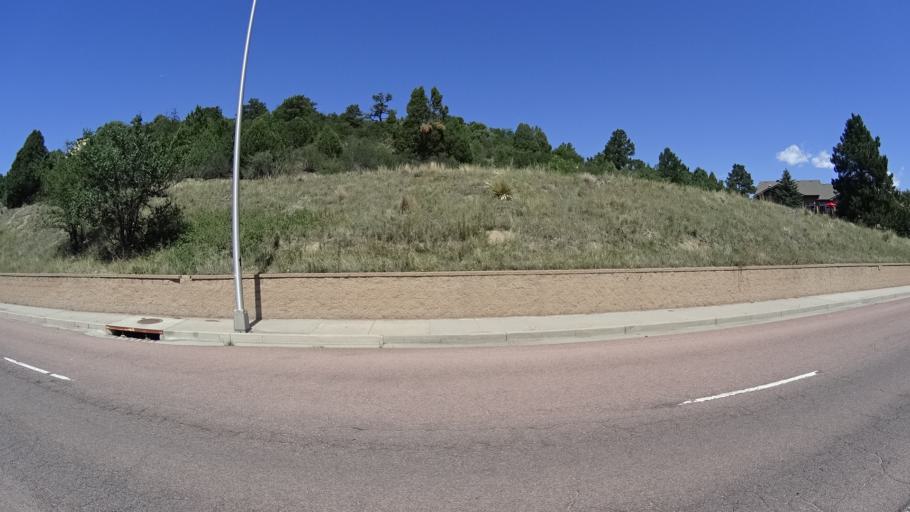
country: US
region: Colorado
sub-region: El Paso County
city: Colorado Springs
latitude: 38.8977
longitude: -104.7823
